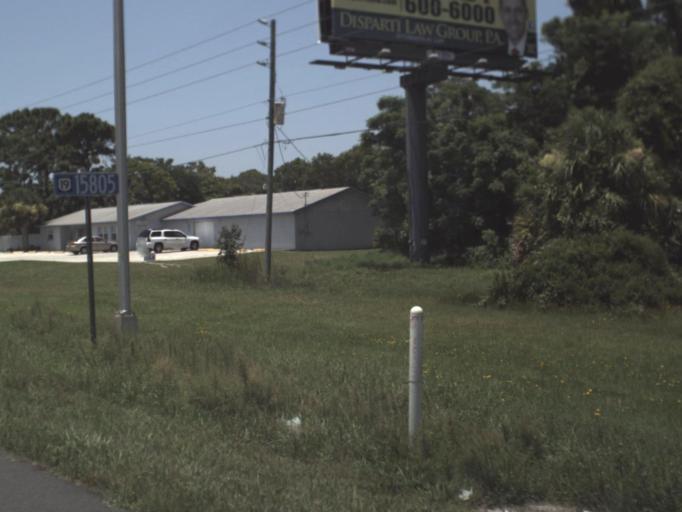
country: US
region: Florida
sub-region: Pasco County
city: Hudson
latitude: 28.3854
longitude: -82.6733
